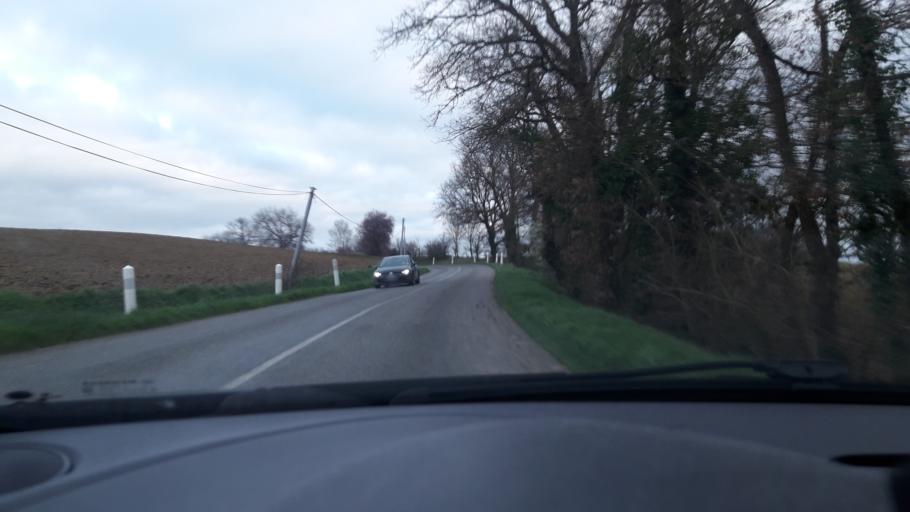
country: FR
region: Midi-Pyrenees
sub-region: Departement de la Haute-Garonne
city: Launac
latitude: 43.6996
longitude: 1.0527
